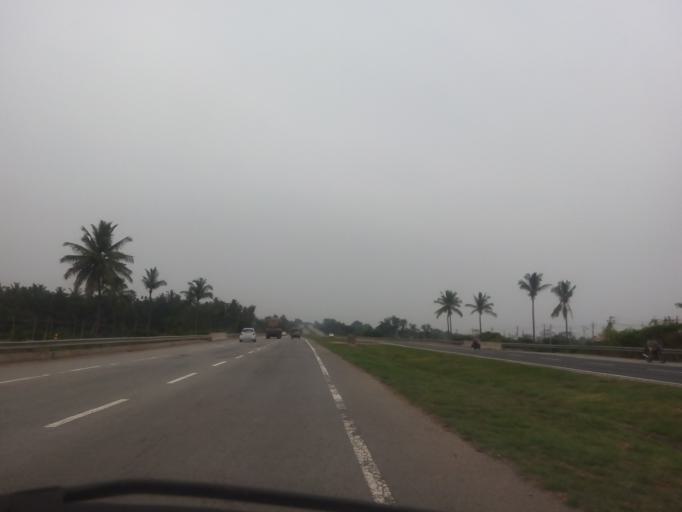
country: IN
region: Karnataka
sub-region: Bangalore Urban
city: Bangalore
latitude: 12.9386
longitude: 77.4695
